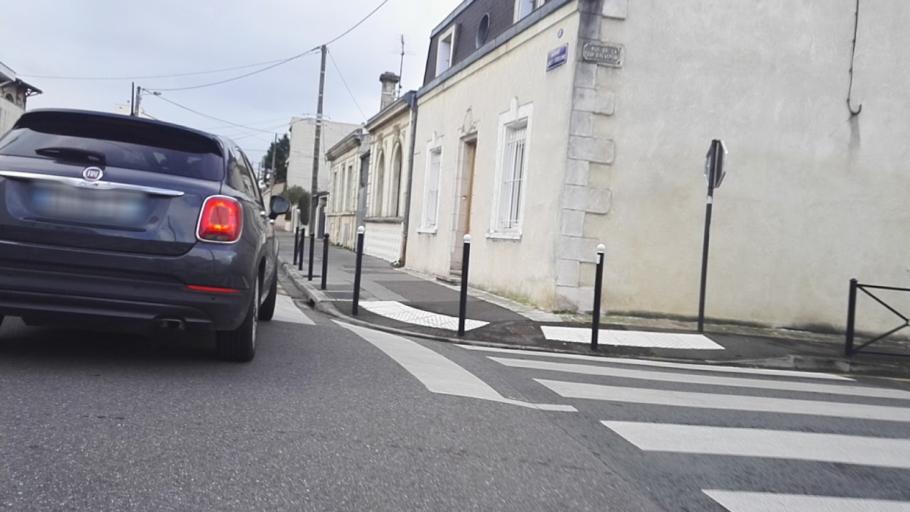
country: FR
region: Aquitaine
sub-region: Departement de la Gironde
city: Le Bouscat
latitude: 44.8470
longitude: -0.6079
